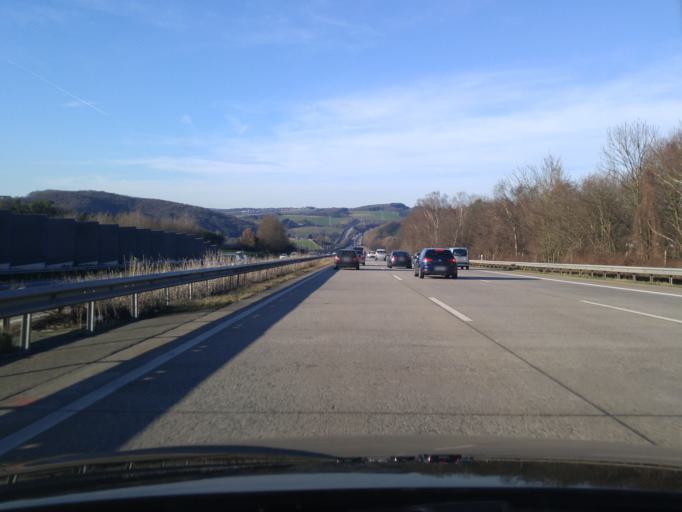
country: DE
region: Rheinland-Pfalz
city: Rossbach
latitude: 50.6157
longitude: 7.4196
